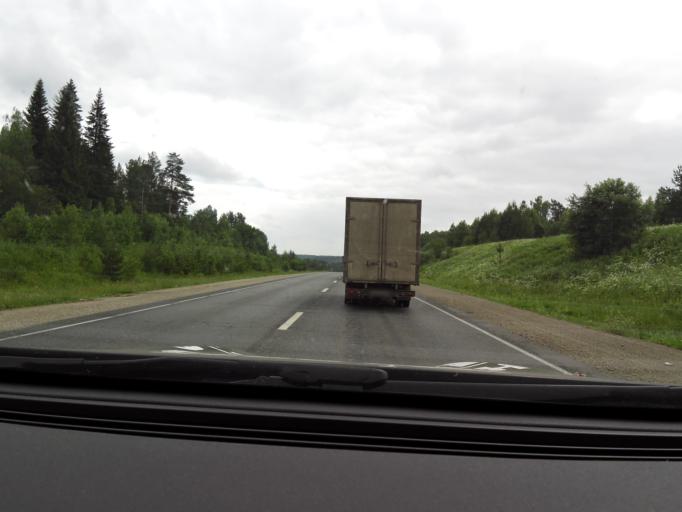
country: RU
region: Perm
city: Suksun
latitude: 57.1329
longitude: 57.2992
